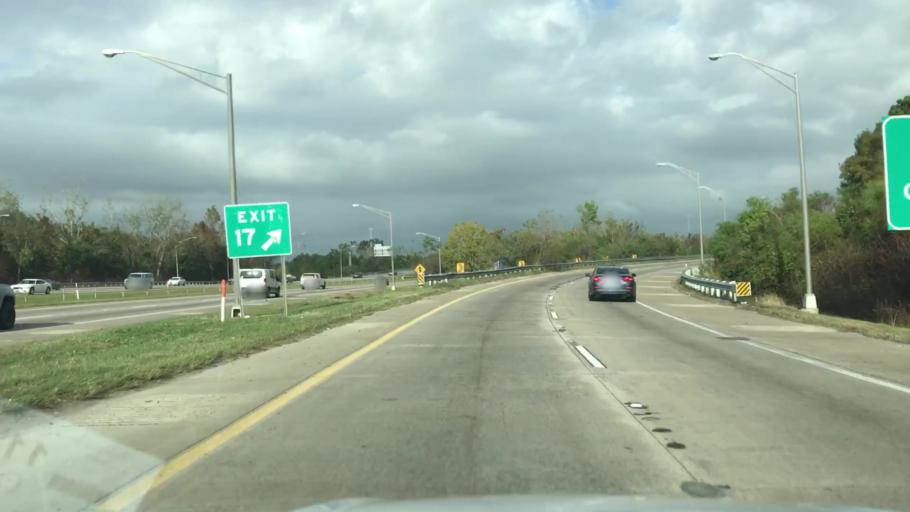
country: US
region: South Carolina
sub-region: Berkeley County
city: Hanahan
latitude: 32.8801
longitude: -80.0236
